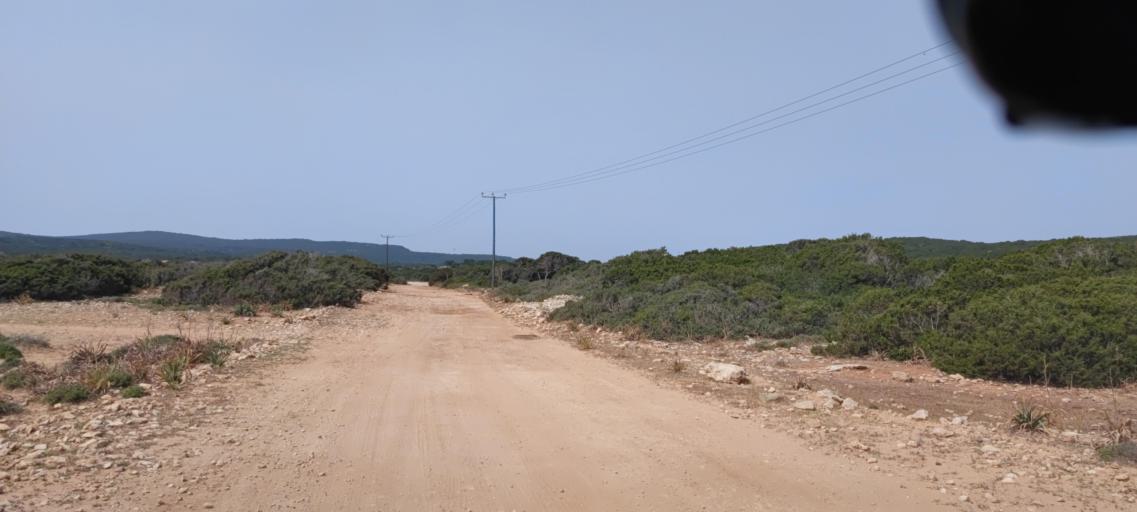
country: CY
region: Ammochostos
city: Rizokarpaso
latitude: 35.6717
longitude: 34.5748
